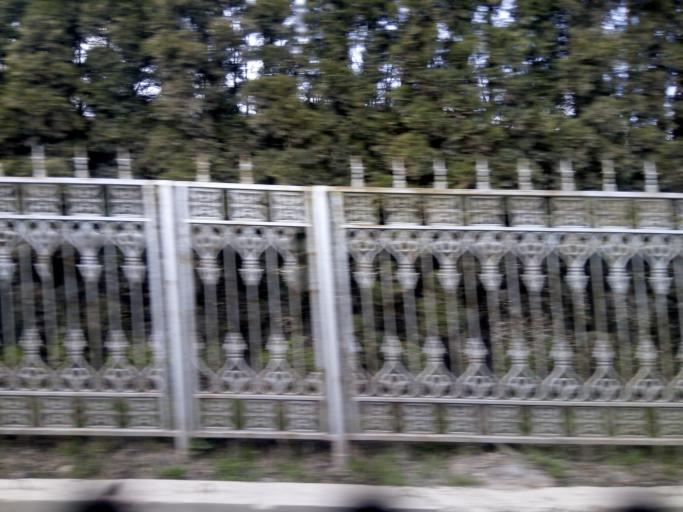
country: RU
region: Moskovskaya
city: Skolkovo
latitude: 55.6884
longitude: 37.3746
